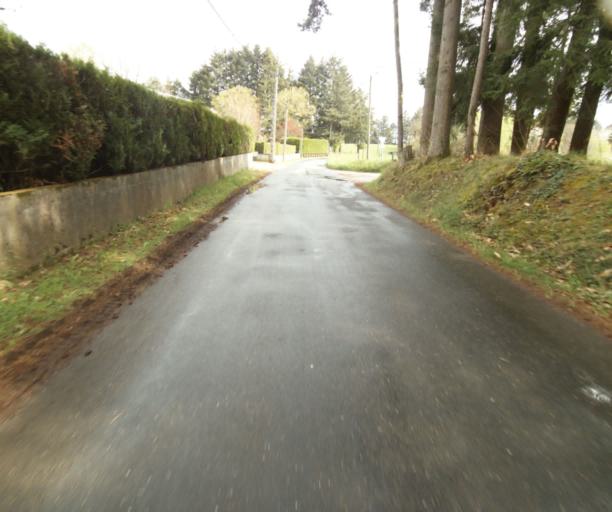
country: FR
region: Limousin
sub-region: Departement de la Correze
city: Tulle
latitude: 45.2890
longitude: 1.7427
